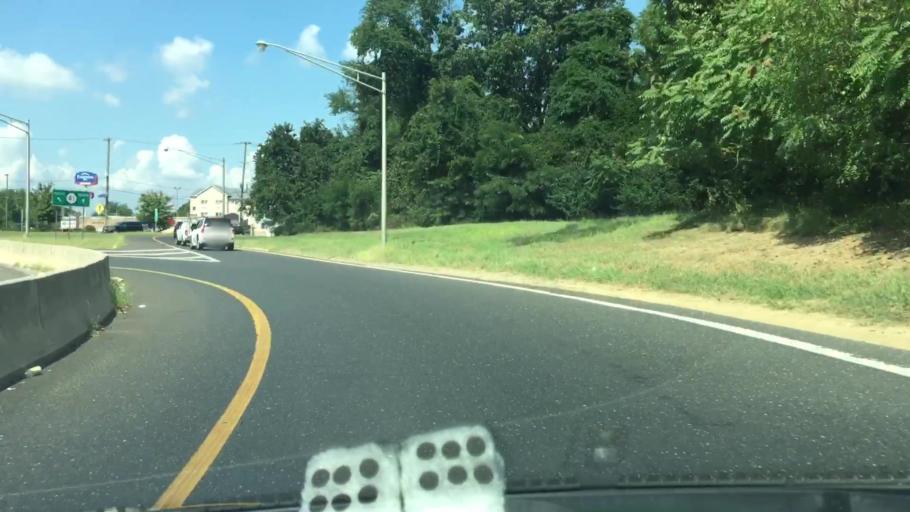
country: US
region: New Jersey
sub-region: Camden County
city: Glendora
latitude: 39.8323
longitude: -75.0876
